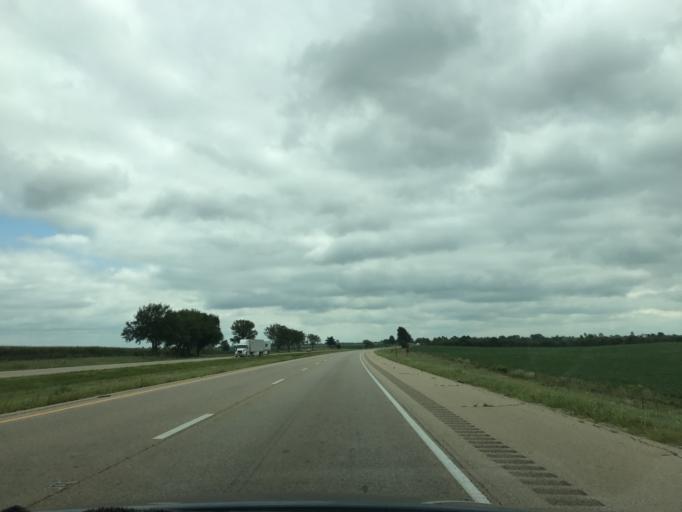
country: US
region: Illinois
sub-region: Bureau County
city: Depue
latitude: 41.4001
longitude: -89.3168
